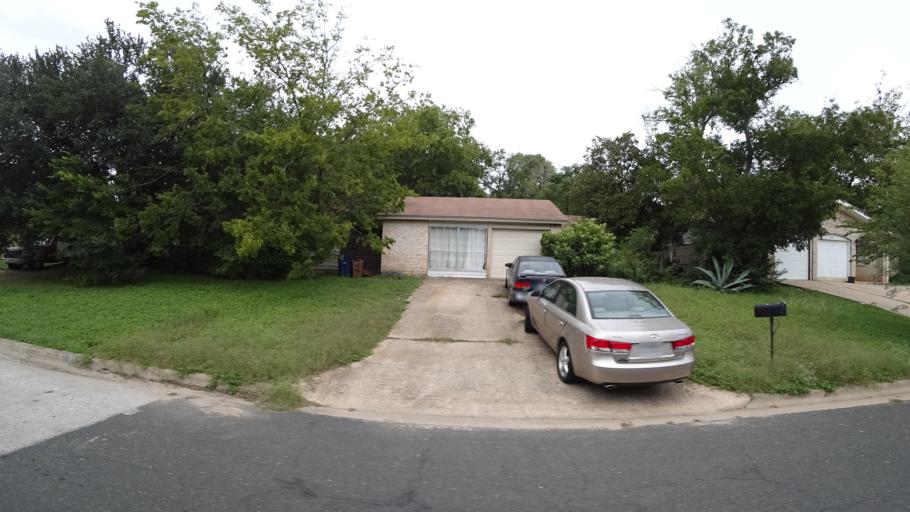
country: US
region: Texas
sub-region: Travis County
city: Rollingwood
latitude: 30.2159
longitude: -97.7872
